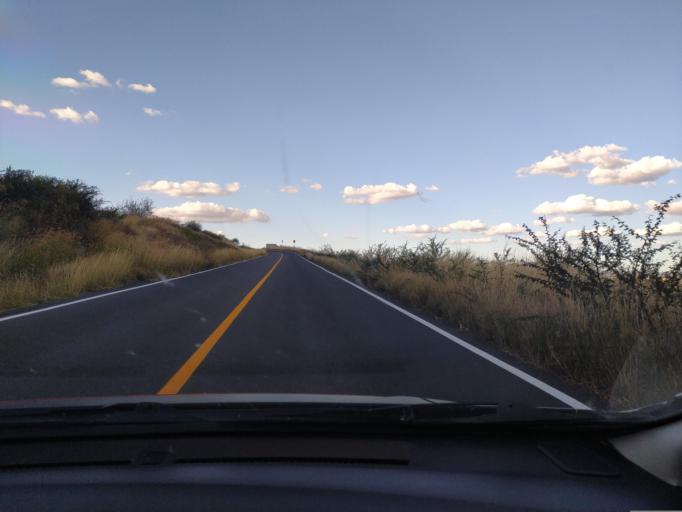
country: MX
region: Guanajuato
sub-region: Purisima del Rincon
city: Monte Grande
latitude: 21.0201
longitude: -101.8961
